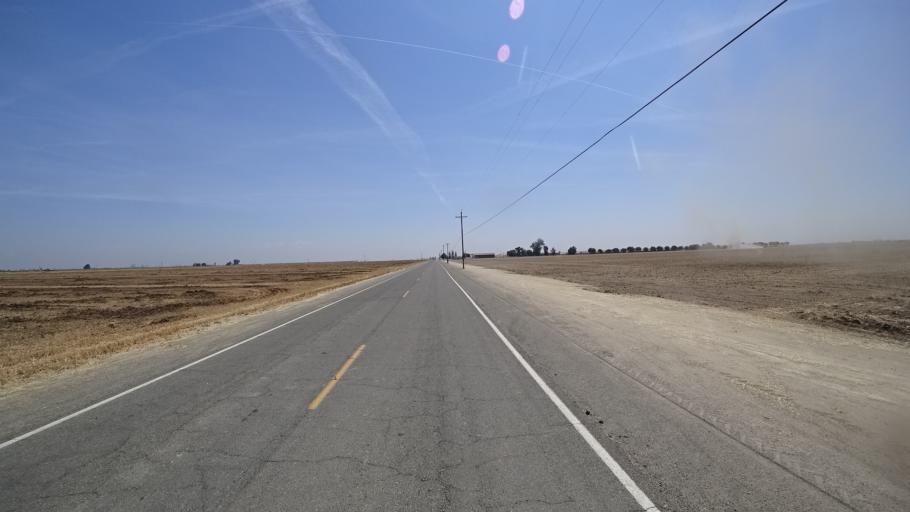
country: US
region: California
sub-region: Fresno County
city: Kingsburg
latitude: 36.4014
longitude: -119.5356
